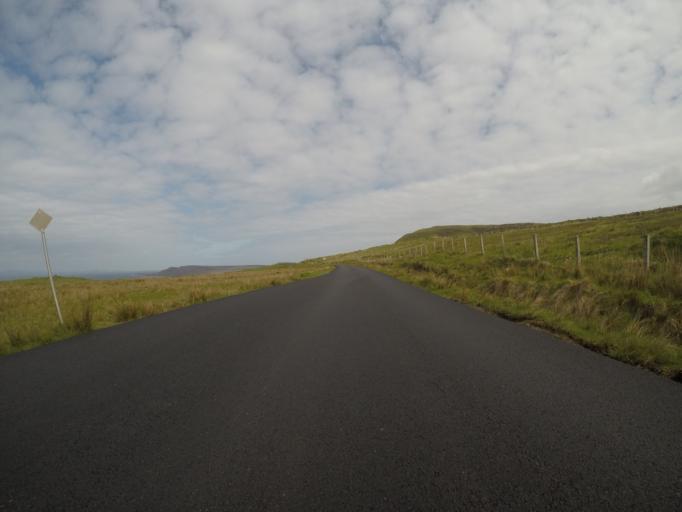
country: GB
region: Scotland
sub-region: Highland
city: Portree
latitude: 57.6618
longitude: -6.3673
